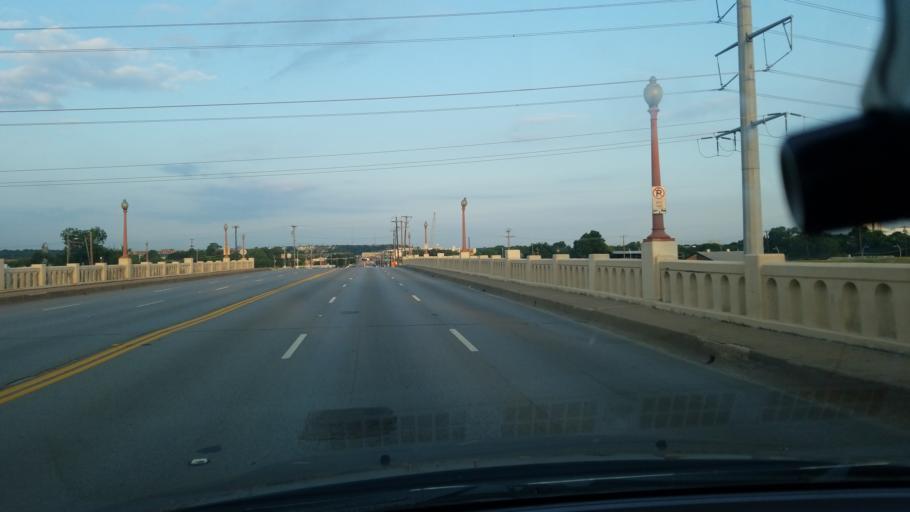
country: US
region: Texas
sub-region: Dallas County
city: Dallas
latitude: 32.7753
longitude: -96.8209
